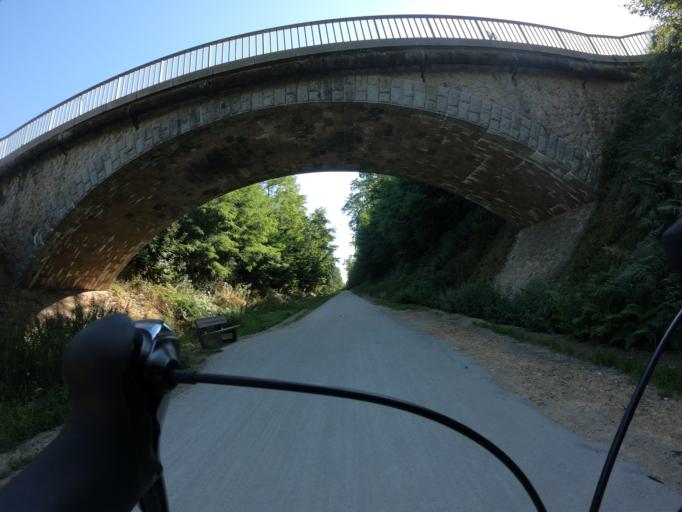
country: FR
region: Lower Normandy
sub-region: Departement de la Manche
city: Parigny
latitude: 48.6078
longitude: -1.0302
